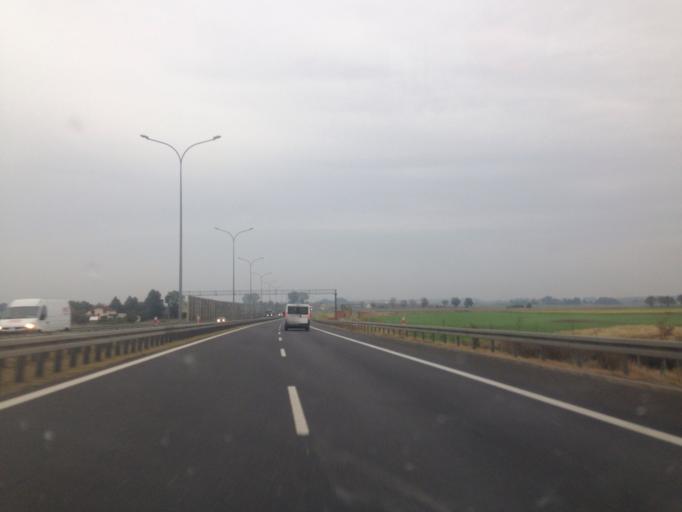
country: PL
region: Greater Poland Voivodeship
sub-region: Powiat poznanski
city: Kostrzyn
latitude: 52.3882
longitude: 17.2506
